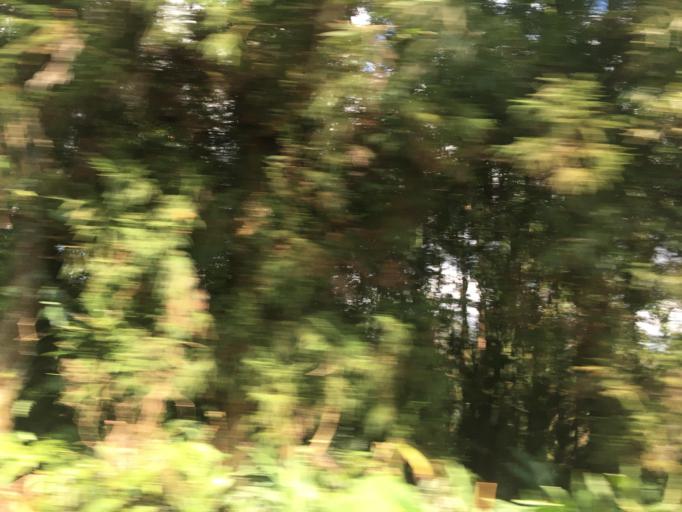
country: TW
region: Taiwan
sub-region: Yilan
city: Yilan
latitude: 24.7543
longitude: 121.6389
